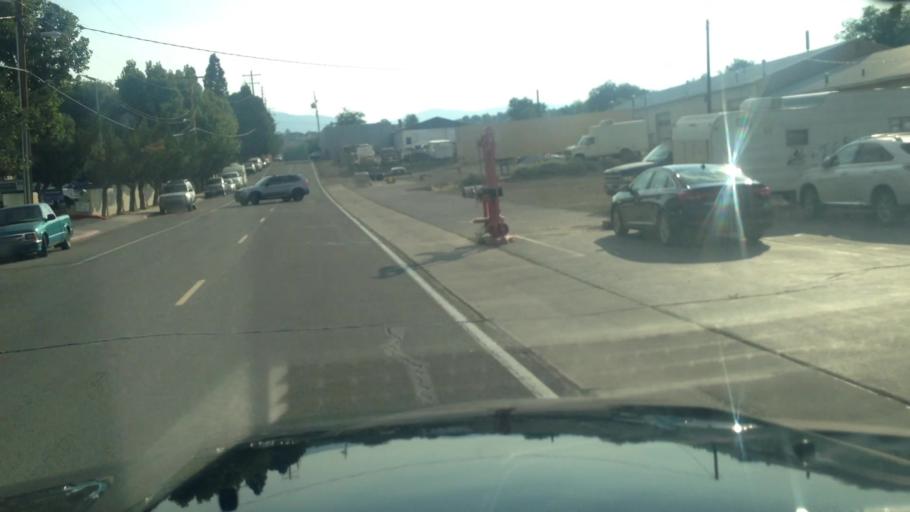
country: US
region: Nevada
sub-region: Washoe County
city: Reno
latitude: 39.5213
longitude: -119.8402
